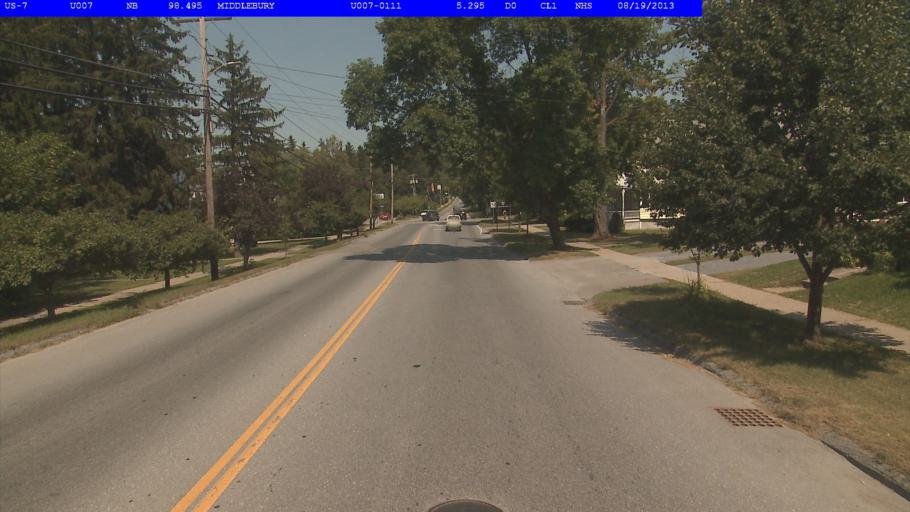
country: US
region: Vermont
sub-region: Addison County
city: Middlebury (village)
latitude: 44.0172
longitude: -73.1669
